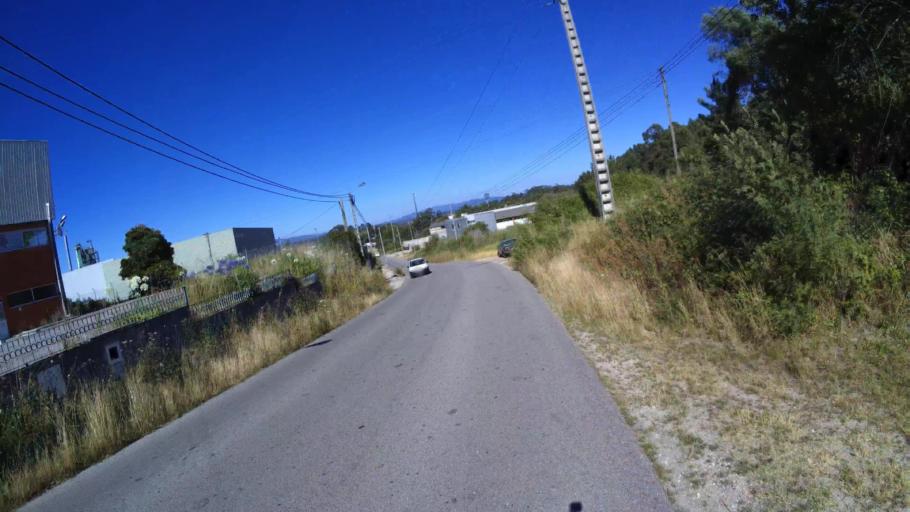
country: PT
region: Aveiro
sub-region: Aveiro
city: Eixo
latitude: 40.6512
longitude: -8.5992
